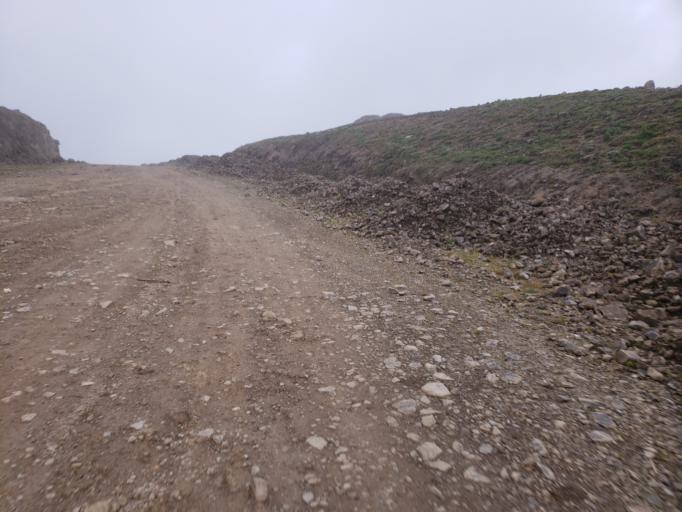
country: ET
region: Oromiya
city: Dodola
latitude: 6.7280
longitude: 39.4287
